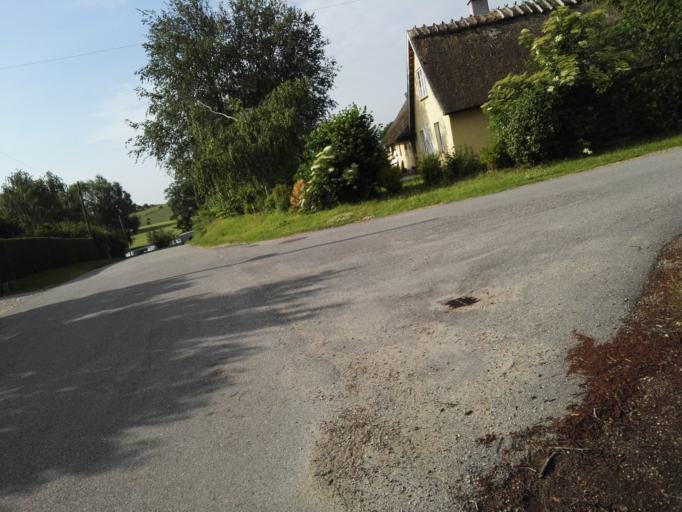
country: DK
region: Zealand
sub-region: Roskilde Kommune
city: Jyllinge
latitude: 55.7979
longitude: 12.1125
